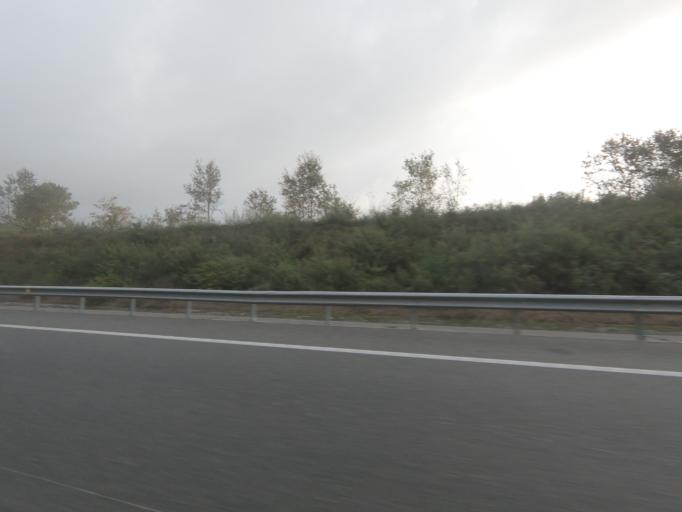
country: ES
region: Galicia
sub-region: Provincia de Pontevedra
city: Porrino
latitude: 42.1861
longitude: -8.6513
